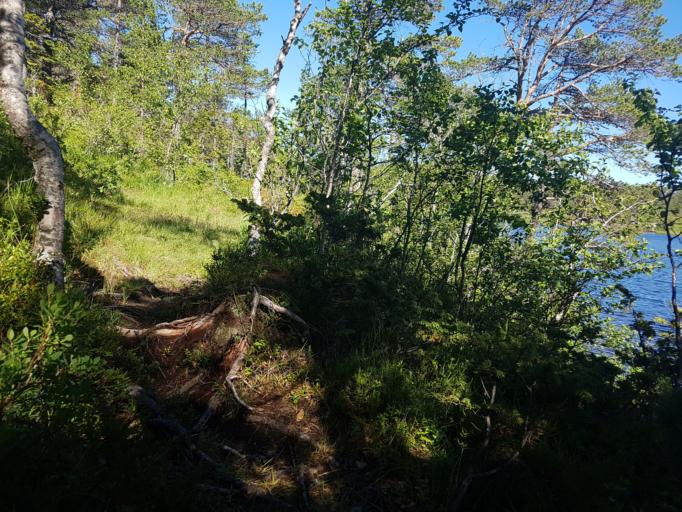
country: NO
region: Sor-Trondelag
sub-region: Trondheim
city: Trondheim
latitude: 63.4410
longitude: 10.2539
